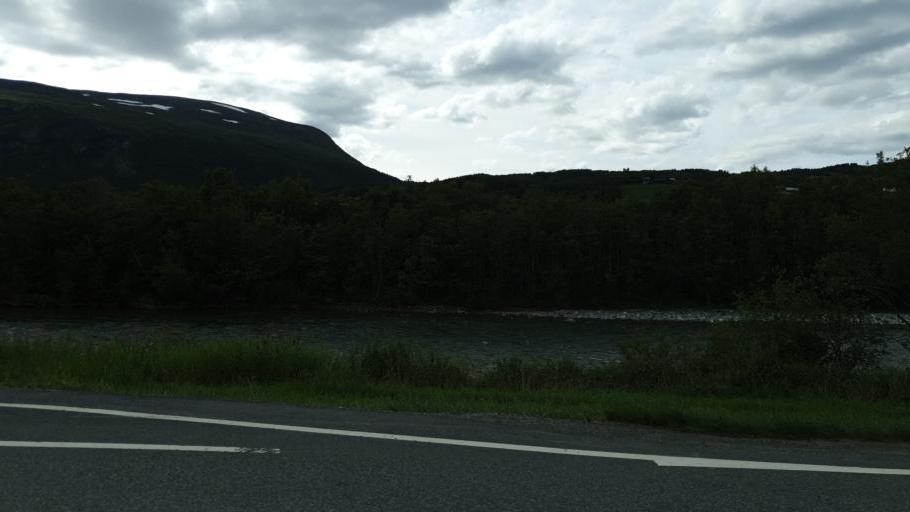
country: NO
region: Sor-Trondelag
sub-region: Oppdal
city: Oppdal
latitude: 62.5565
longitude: 9.6350
